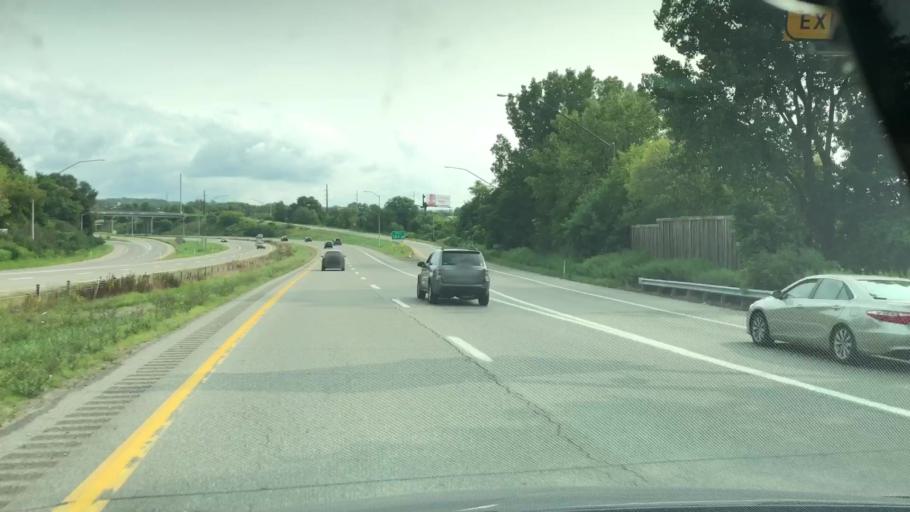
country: US
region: Pennsylvania
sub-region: Erie County
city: Erie
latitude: 42.0987
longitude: -80.1221
